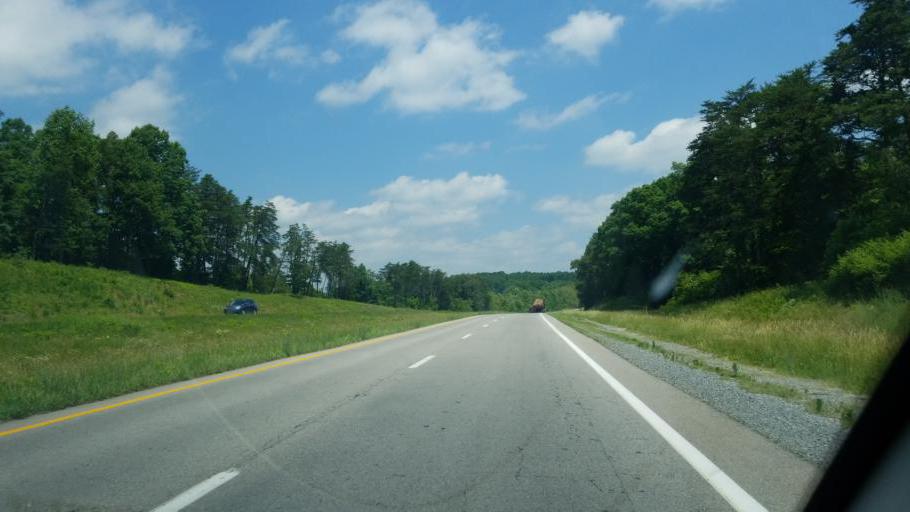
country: US
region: Virginia
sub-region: Pittsylvania County
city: Motley
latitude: 37.0999
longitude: -79.3324
